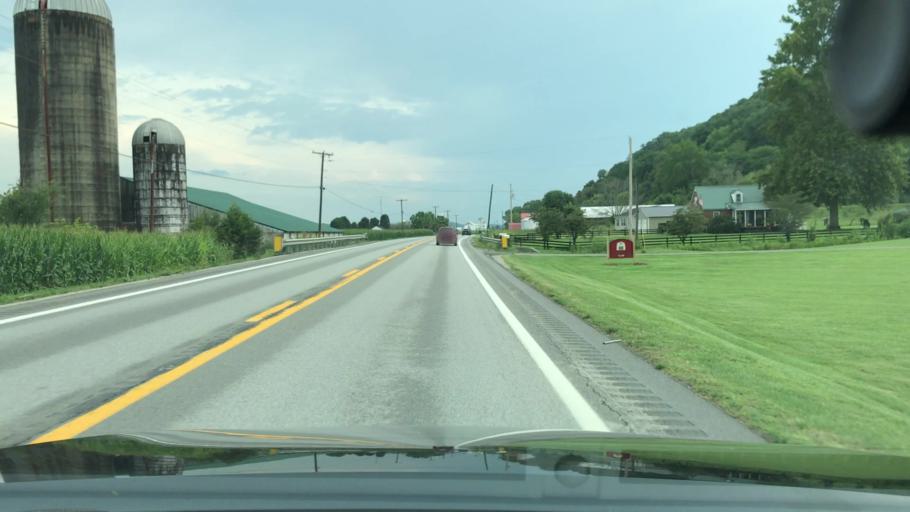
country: US
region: West Virginia
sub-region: Putnam County
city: Buffalo
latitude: 38.7353
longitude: -81.9748
